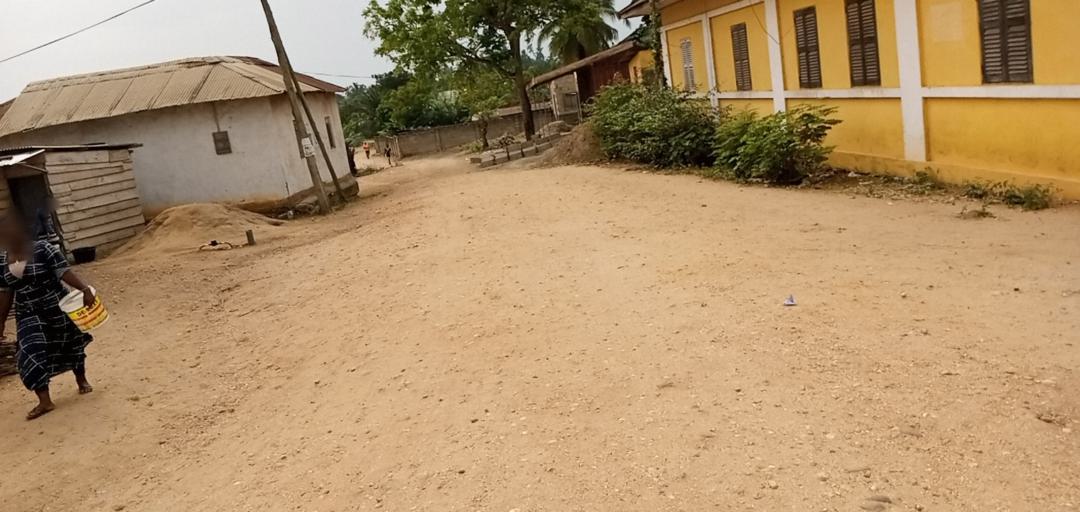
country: GH
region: Central
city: Winneba
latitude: 5.3532
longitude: -0.6278
